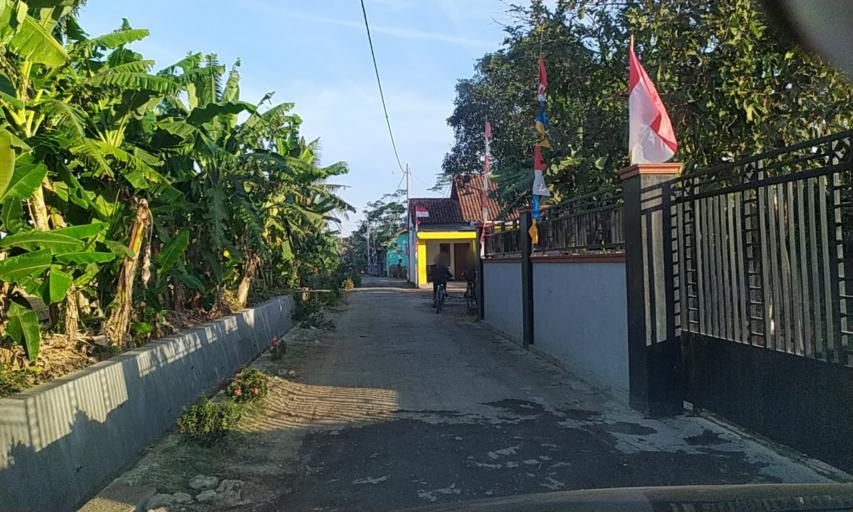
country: ID
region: Central Java
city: Rejanegara
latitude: -7.6910
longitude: 109.0434
